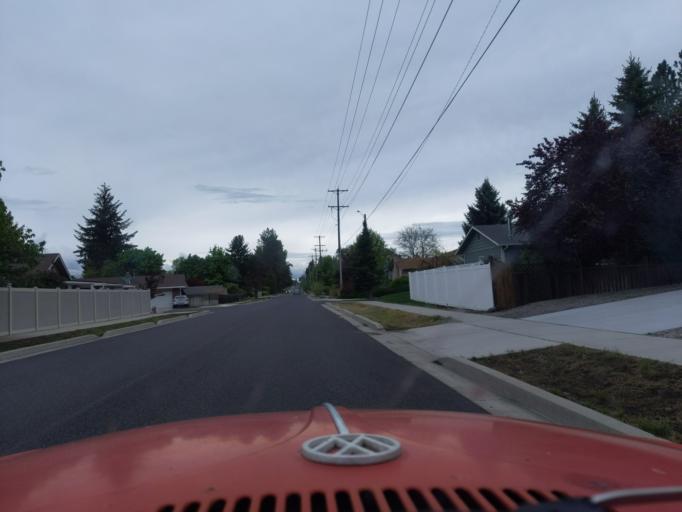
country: US
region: Washington
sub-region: Spokane County
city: Spokane
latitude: 47.6109
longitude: -117.3790
